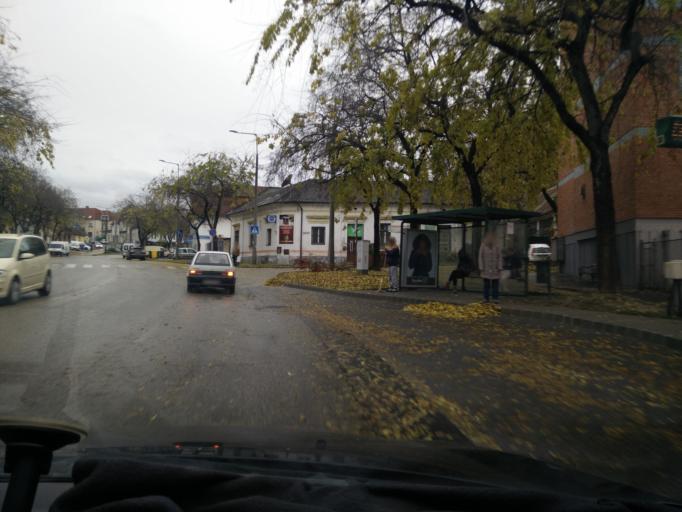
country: HU
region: Tolna
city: Szekszard
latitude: 46.3517
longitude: 18.7006
